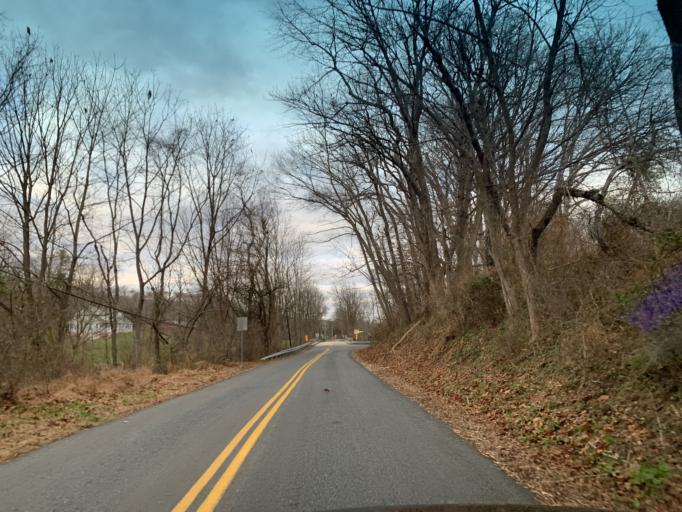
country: US
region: Maryland
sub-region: Harford County
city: Jarrettsville
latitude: 39.6508
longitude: -76.4372
